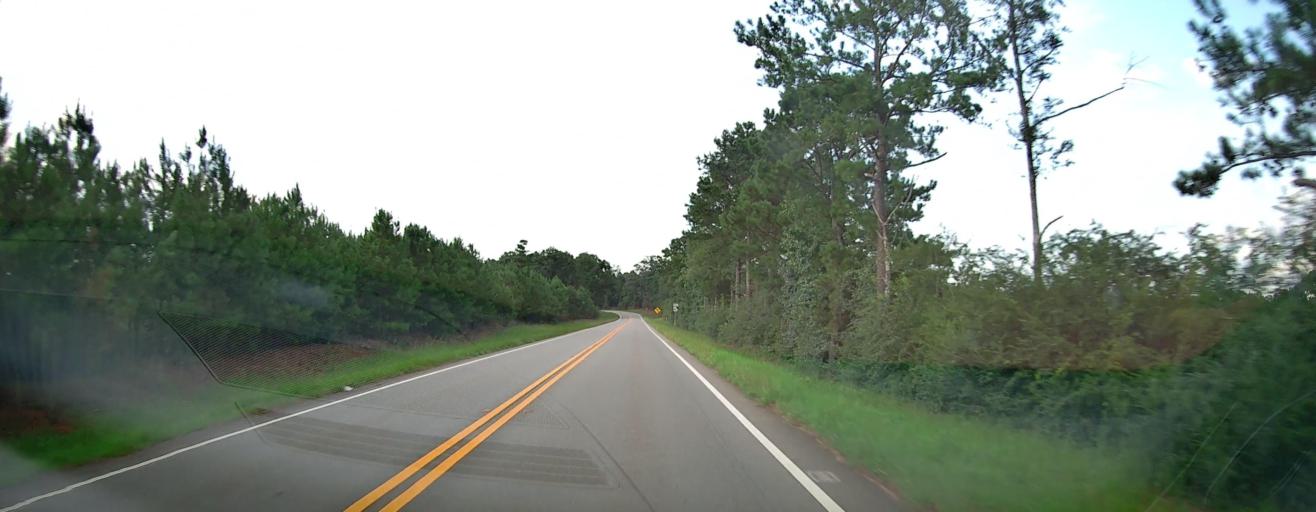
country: US
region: Georgia
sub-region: Monroe County
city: Forsyth
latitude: 33.0006
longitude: -83.9406
